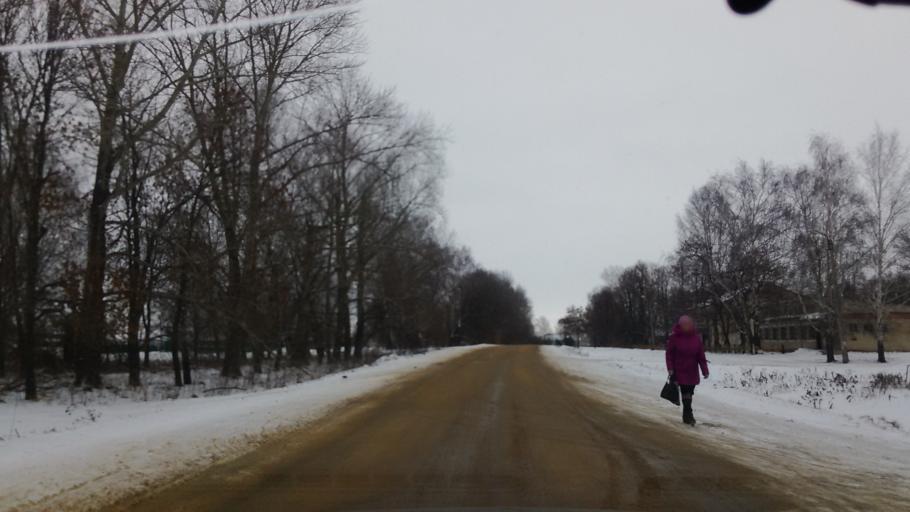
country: RU
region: Tula
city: Bogoroditsk
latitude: 53.7628
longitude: 37.9876
